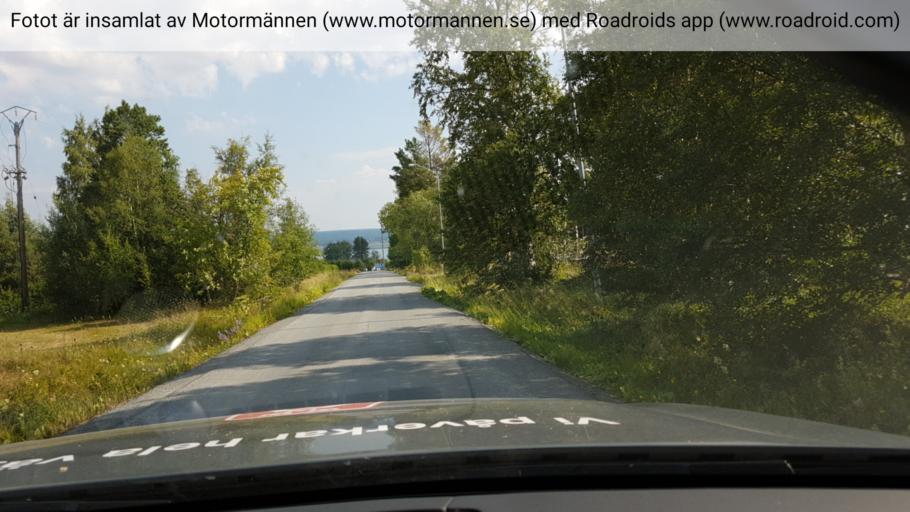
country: SE
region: Jaemtland
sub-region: OEstersunds Kommun
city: Ostersund
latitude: 63.1297
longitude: 14.6381
